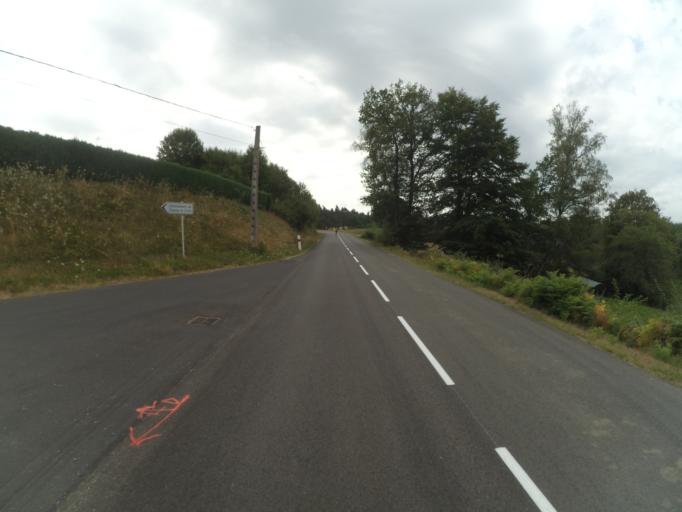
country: FR
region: Limousin
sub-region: Departement de la Creuse
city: La Courtine
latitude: 45.6630
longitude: 2.2014
